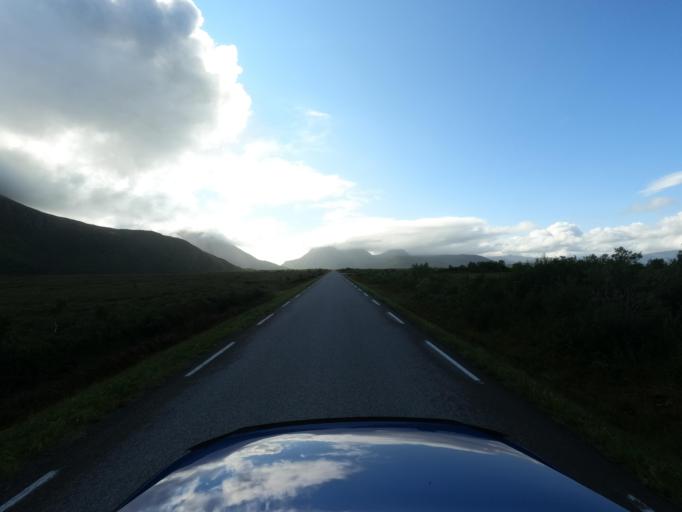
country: NO
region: Nordland
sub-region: Vagan
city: Kabelvag
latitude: 68.3058
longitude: 14.1796
